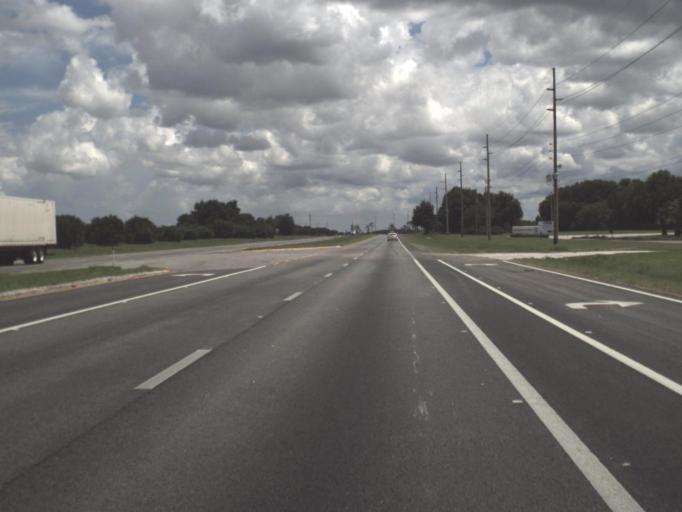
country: US
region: Florida
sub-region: Polk County
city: Alturas
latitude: 27.9017
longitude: -81.6548
